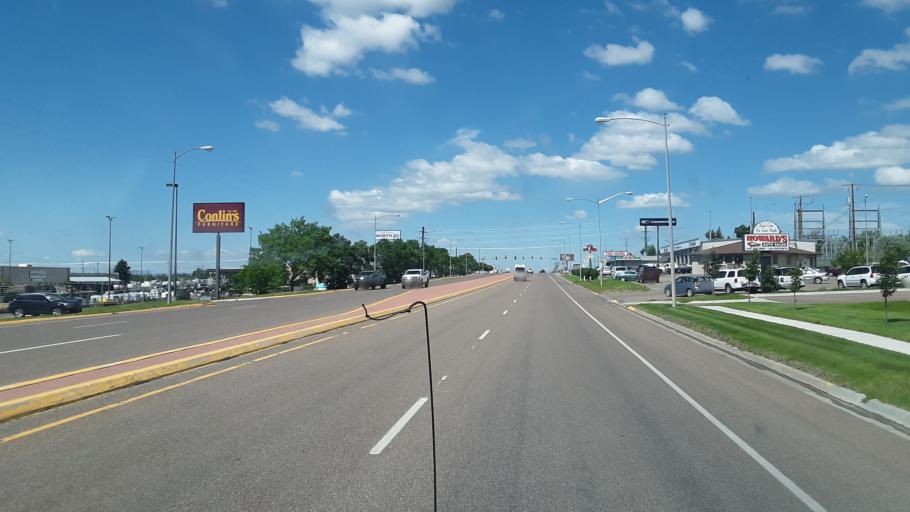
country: US
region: Montana
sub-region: Cascade County
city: Malmstrom Air Force Base
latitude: 47.4940
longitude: -111.2289
